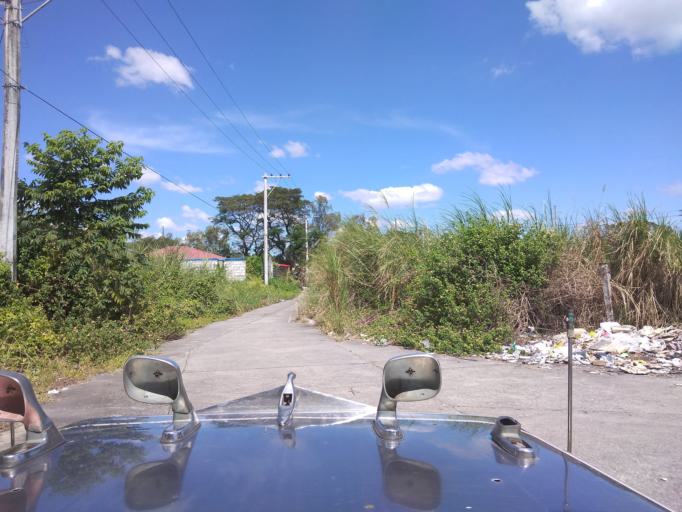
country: PH
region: Central Luzon
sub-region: Province of Pampanga
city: Calibutbut
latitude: 15.1142
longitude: 120.5959
